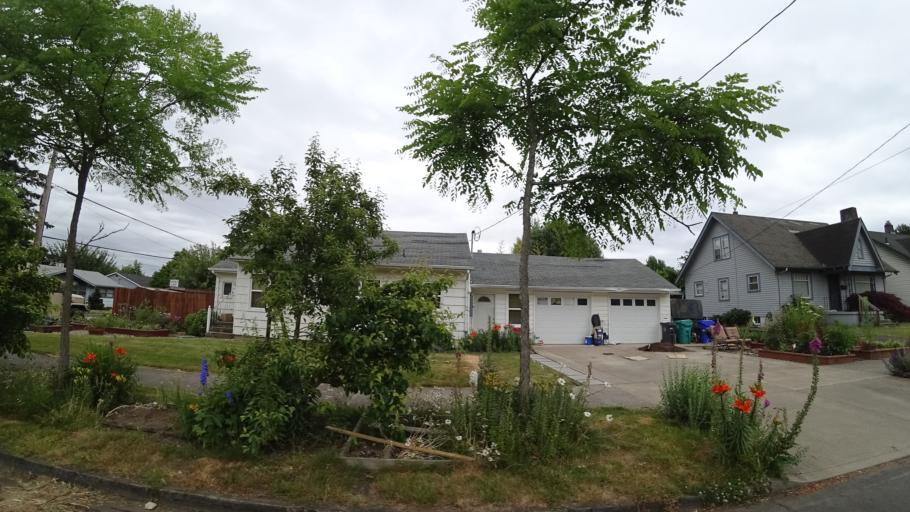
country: US
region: Oregon
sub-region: Multnomah County
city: Portland
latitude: 45.5824
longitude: -122.7054
